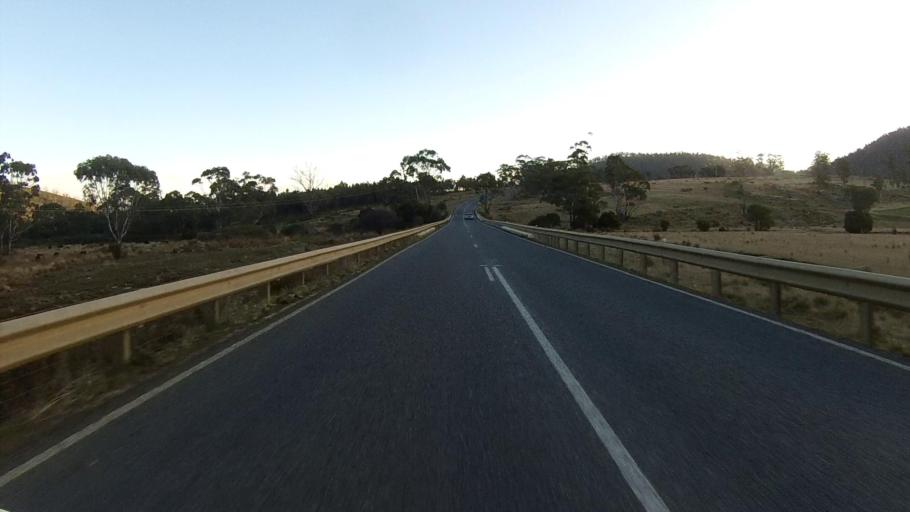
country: AU
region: Tasmania
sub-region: Sorell
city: Sorell
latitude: -42.8153
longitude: 147.7637
